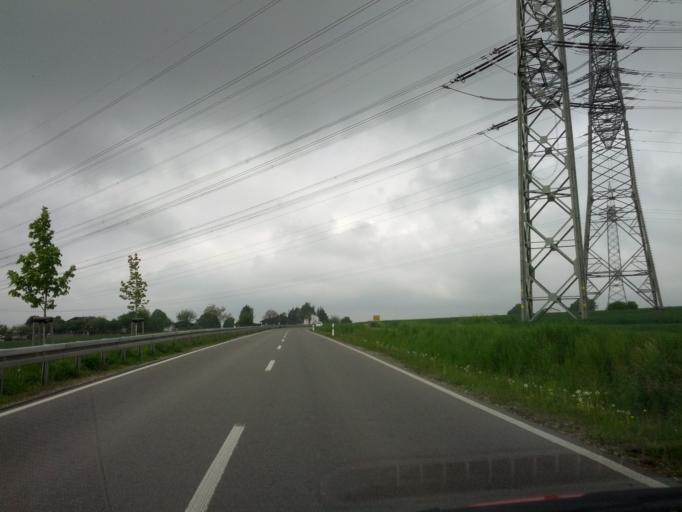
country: DE
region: Baden-Wuerttemberg
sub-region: Regierungsbezirk Stuttgart
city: Magstadt
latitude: 48.7224
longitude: 8.9554
